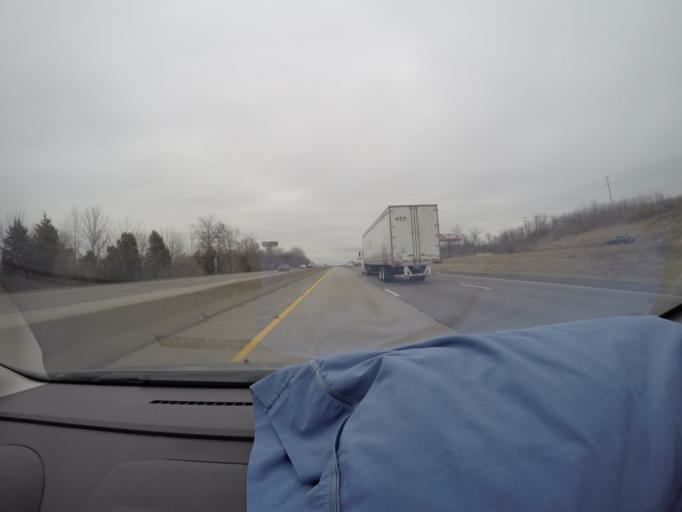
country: US
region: Missouri
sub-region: Saint Charles County
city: Dardenne Prairie
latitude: 38.8033
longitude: -90.7429
